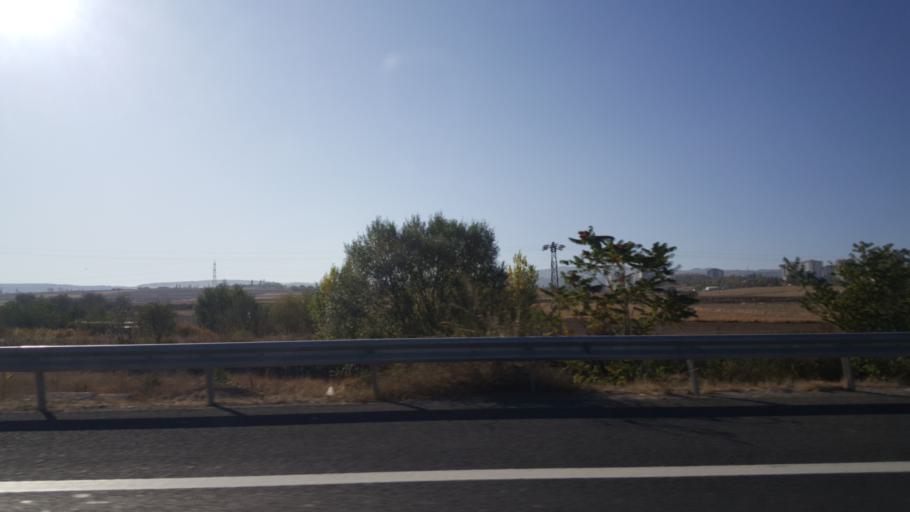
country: TR
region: Ankara
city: Mamak
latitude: 39.9022
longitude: 32.9905
